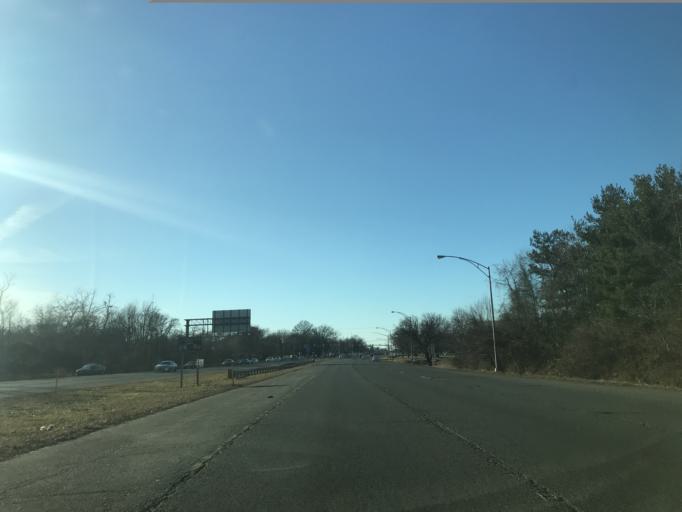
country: US
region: Maryland
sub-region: Prince George's County
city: Forestville
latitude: 38.8405
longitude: -76.8704
